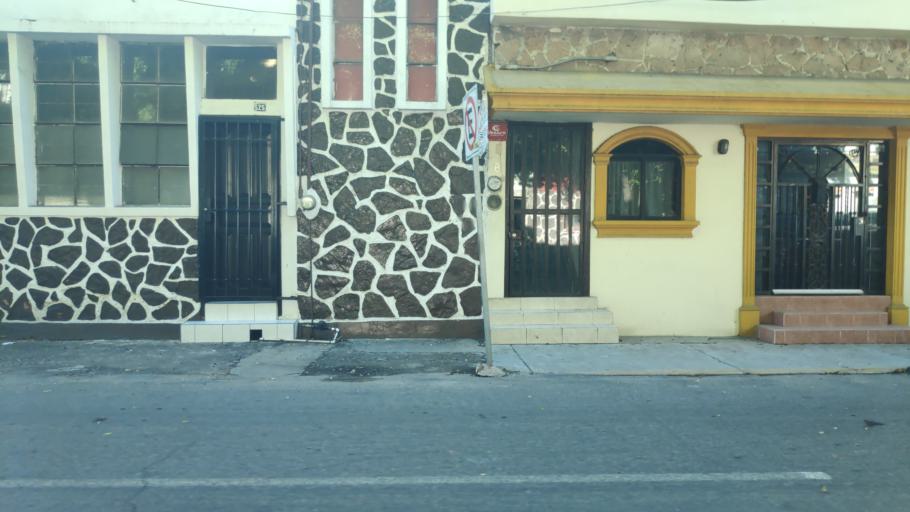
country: MX
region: Sinaloa
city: Culiacan
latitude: 24.8086
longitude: -107.4042
